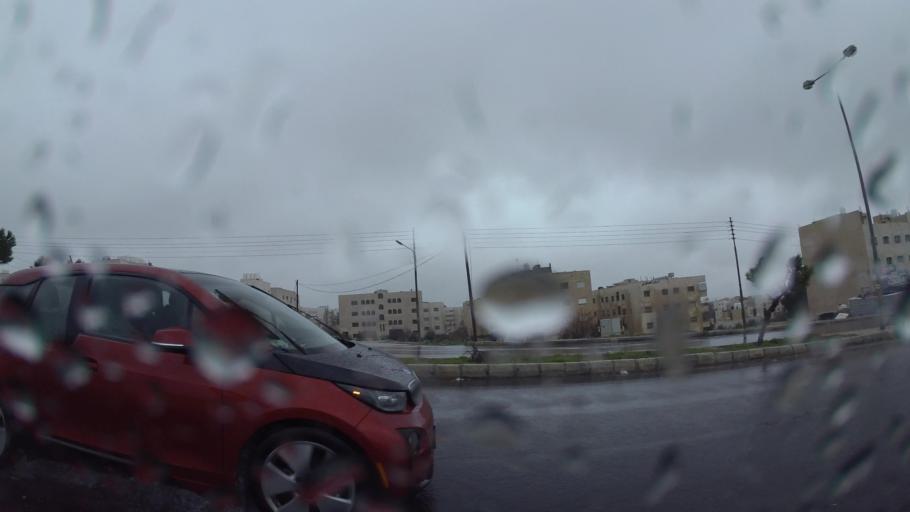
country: JO
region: Amman
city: Al Jubayhah
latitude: 32.0456
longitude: 35.8955
